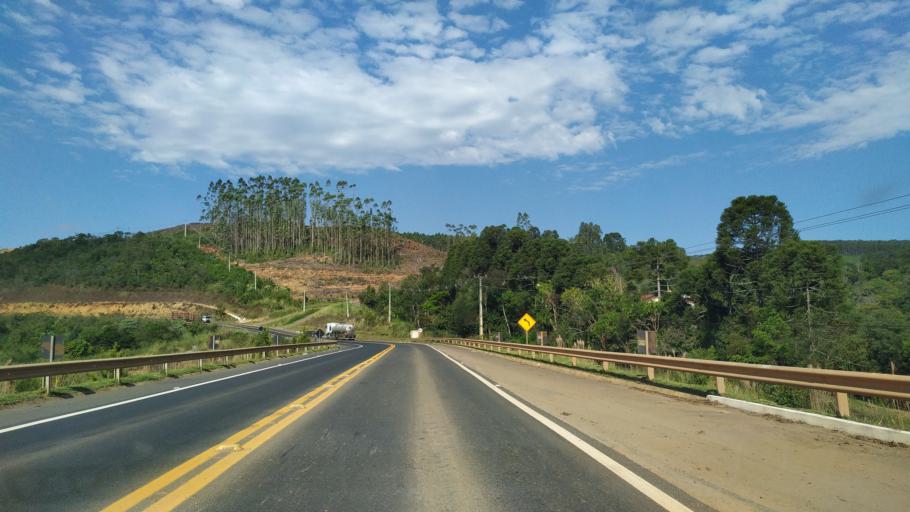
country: BR
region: Parana
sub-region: Telemaco Borba
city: Telemaco Borba
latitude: -24.2650
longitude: -50.7232
